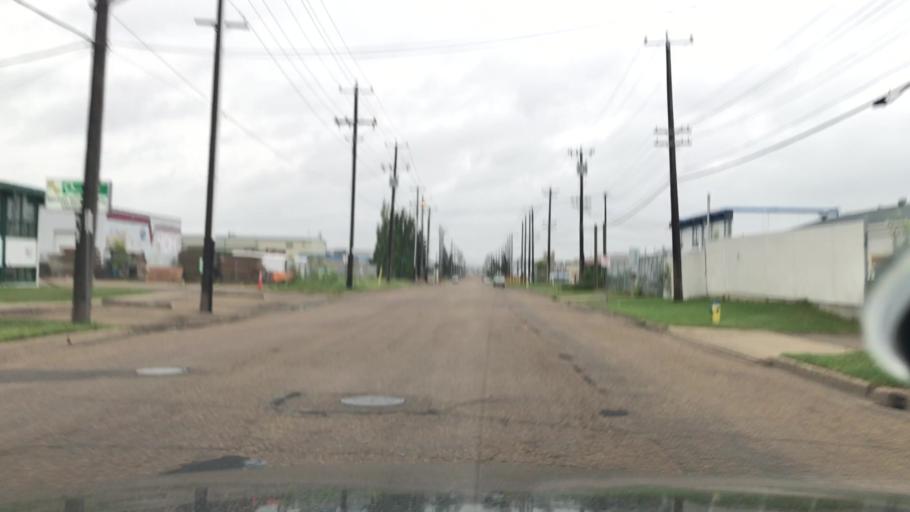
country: CA
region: Alberta
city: Edmonton
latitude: 53.5037
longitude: -113.4494
